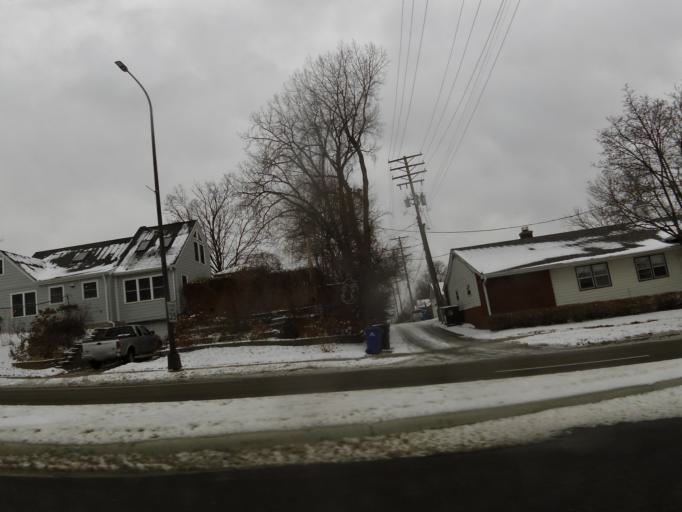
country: US
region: Minnesota
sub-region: Dakota County
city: Mendota Heights
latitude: 44.9192
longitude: -93.1670
